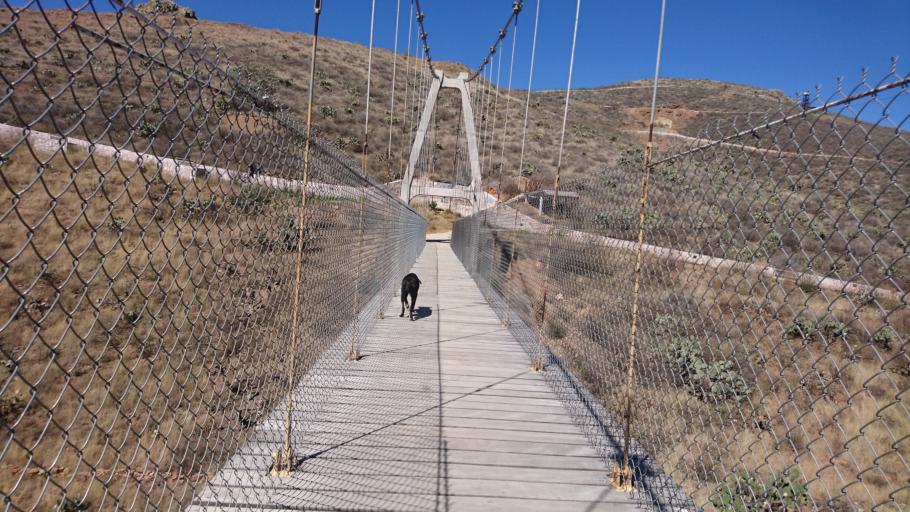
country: MX
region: Zacatecas
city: Guadalupe
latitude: 22.7769
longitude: -102.5456
